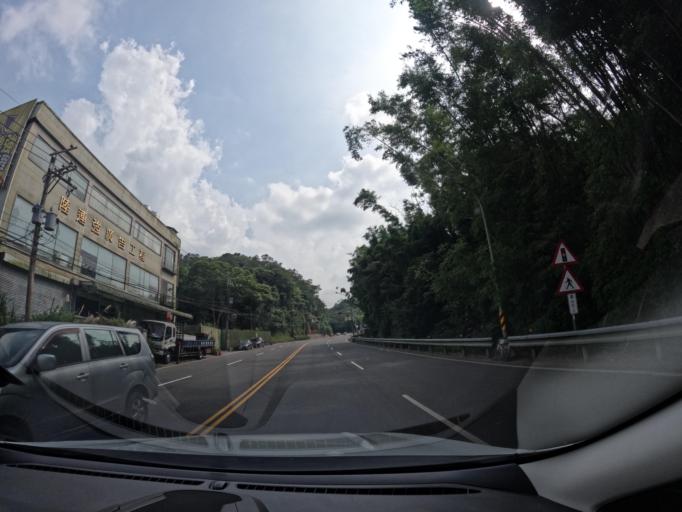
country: TW
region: Taiwan
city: Daxi
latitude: 24.8985
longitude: 121.3383
